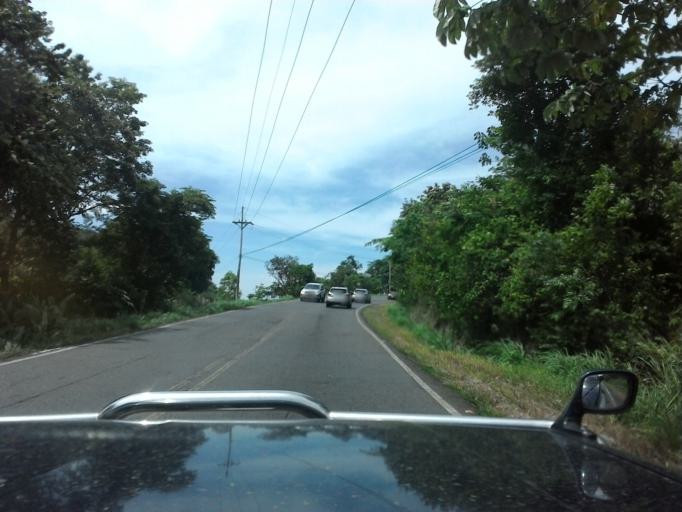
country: CR
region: Puntarenas
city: Esparza
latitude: 10.0177
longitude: -84.6107
